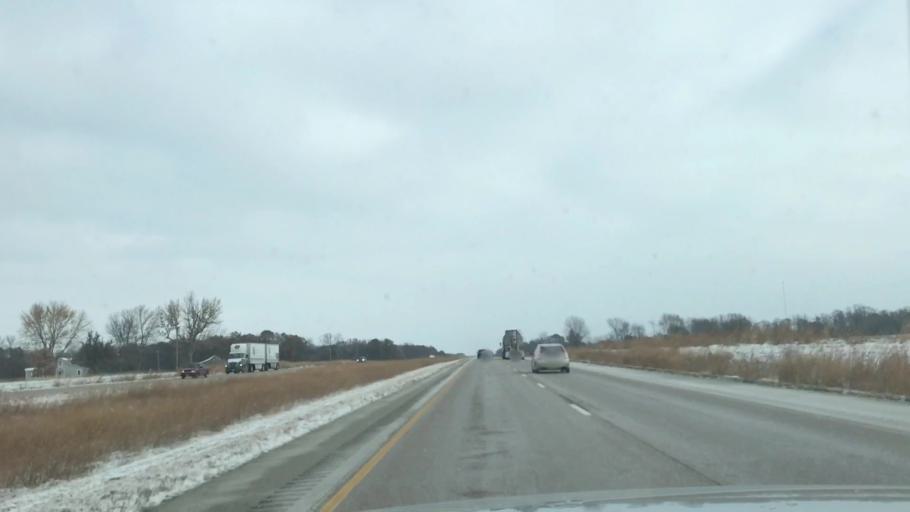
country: US
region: Illinois
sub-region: Macoupin County
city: Mount Olive
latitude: 39.1056
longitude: -89.7305
